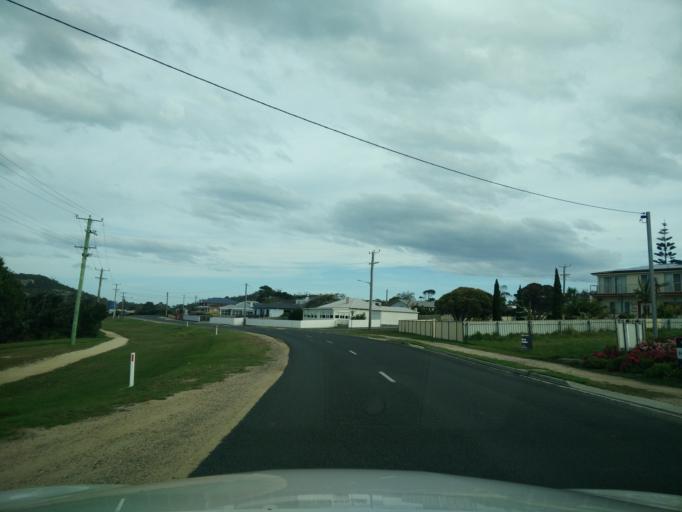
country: AU
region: Tasmania
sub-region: Break O'Day
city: St Helens
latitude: -41.8719
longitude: 148.2961
